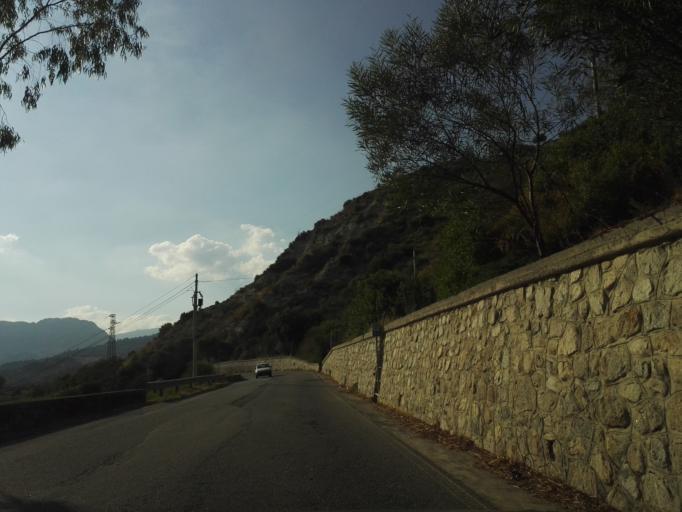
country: IT
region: Calabria
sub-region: Provincia di Reggio Calabria
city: Monasterace
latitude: 38.4615
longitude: 16.5197
